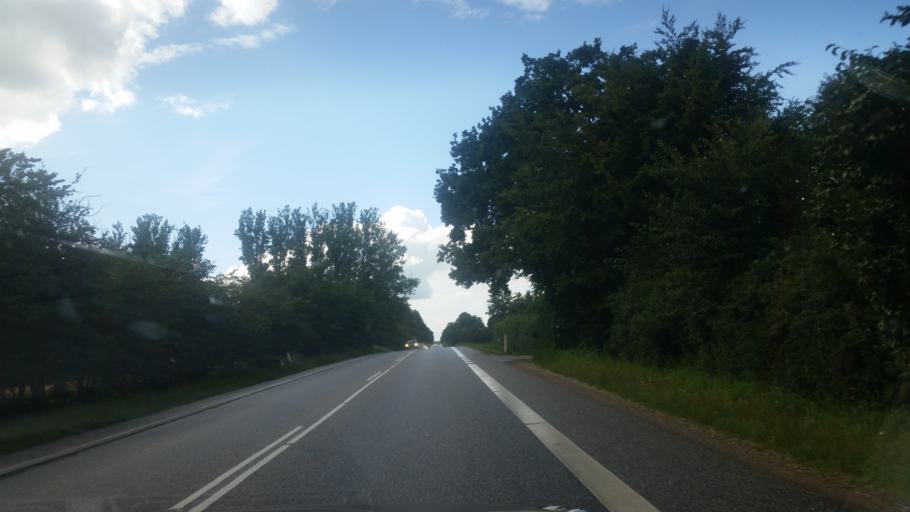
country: DK
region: Zealand
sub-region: Holbaek Kommune
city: Holbaek
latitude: 55.7205
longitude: 11.6032
